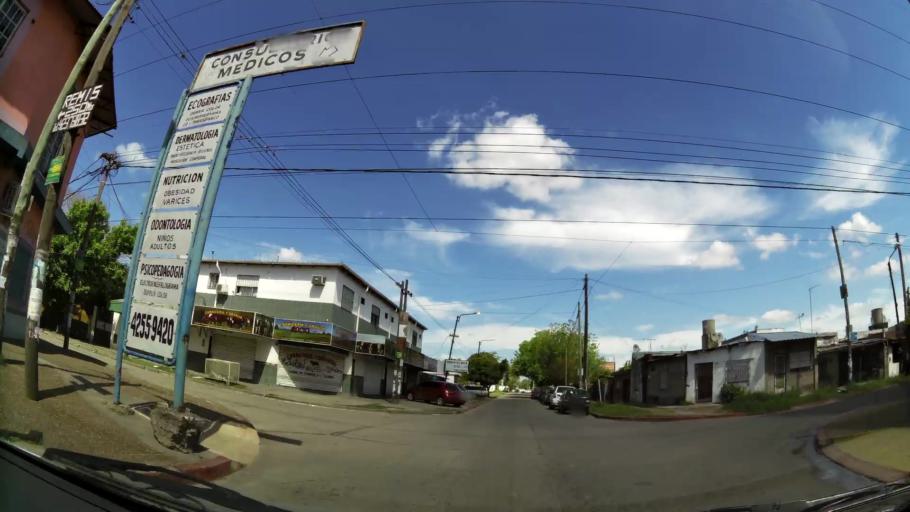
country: AR
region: Buenos Aires
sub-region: Partido de Quilmes
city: Quilmes
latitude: -34.8200
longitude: -58.2713
